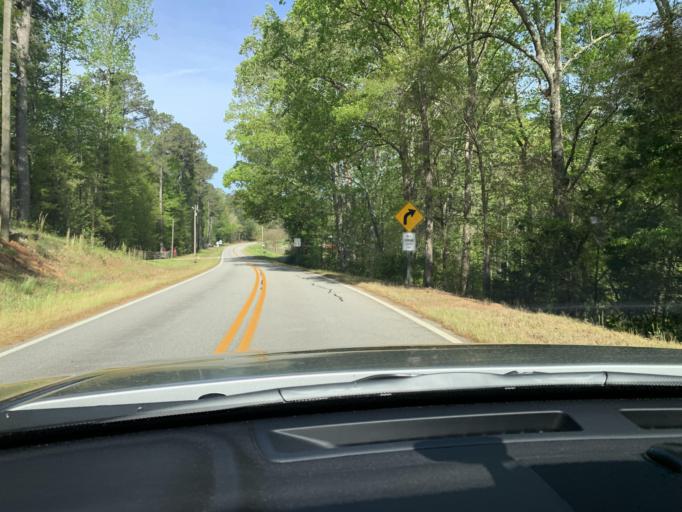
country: US
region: Georgia
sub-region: Oconee County
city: Watkinsville
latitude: 33.8165
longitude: -83.3186
